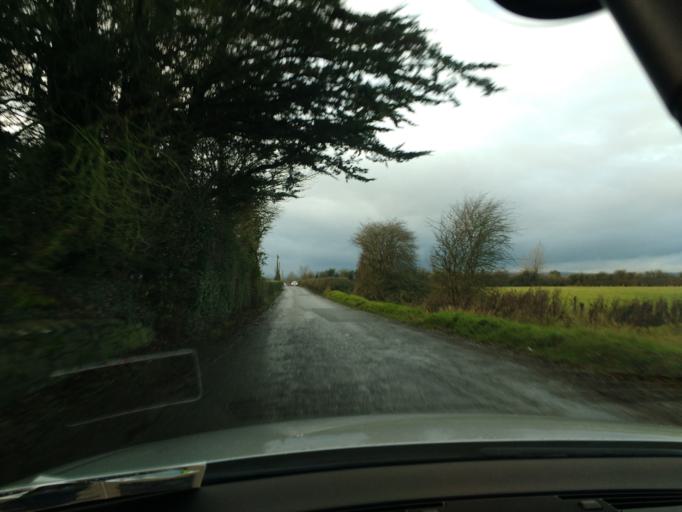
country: IE
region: Munster
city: Thurles
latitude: 52.6348
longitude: -7.8243
